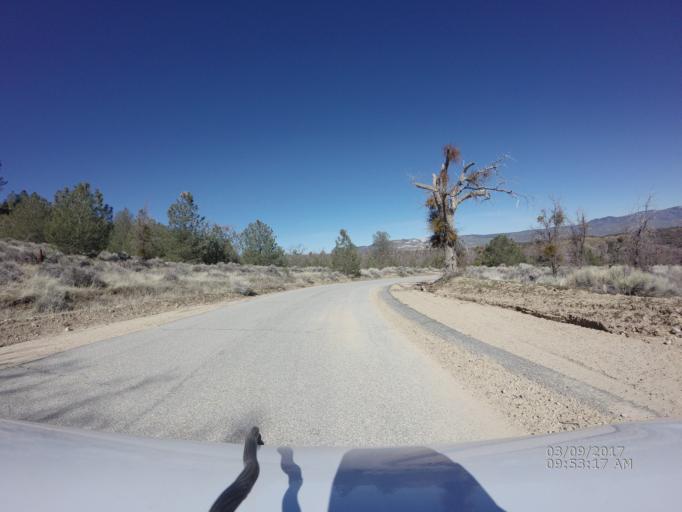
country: US
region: California
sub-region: Kern County
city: Lebec
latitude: 34.7505
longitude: -118.6982
